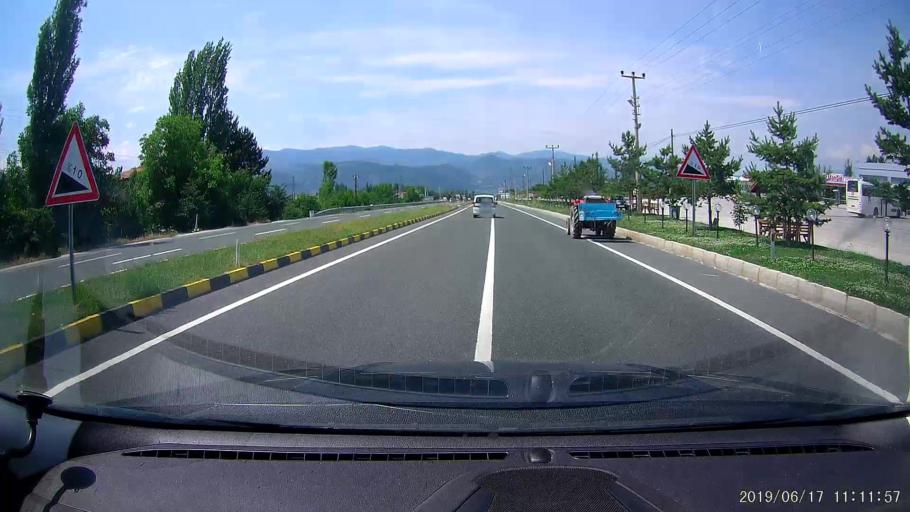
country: TR
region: Kastamonu
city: Tosya
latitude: 40.9794
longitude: 34.0027
